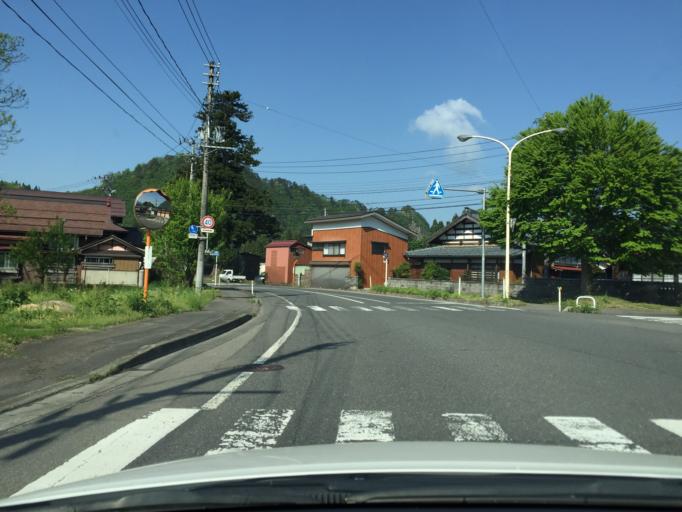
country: JP
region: Niigata
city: Suibara
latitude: 37.6851
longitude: 139.4732
